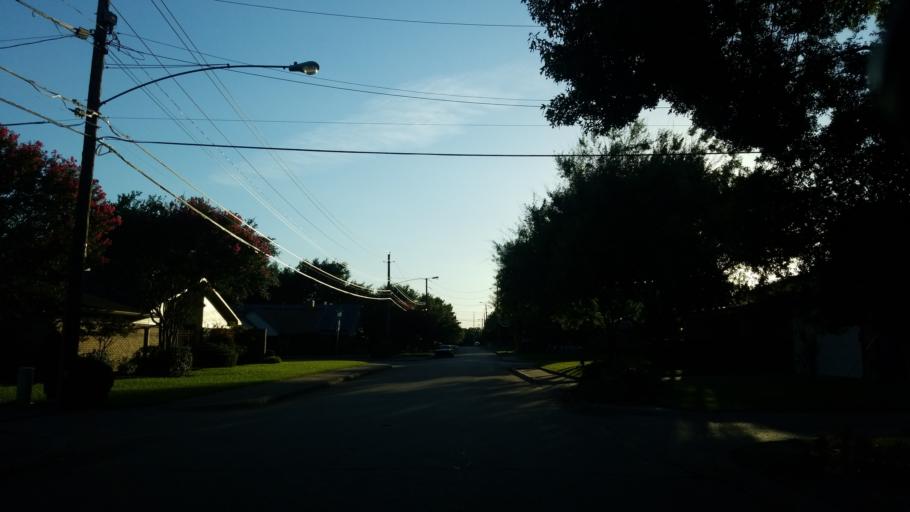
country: US
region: Texas
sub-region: Dallas County
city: Balch Springs
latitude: 32.7885
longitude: -96.6959
